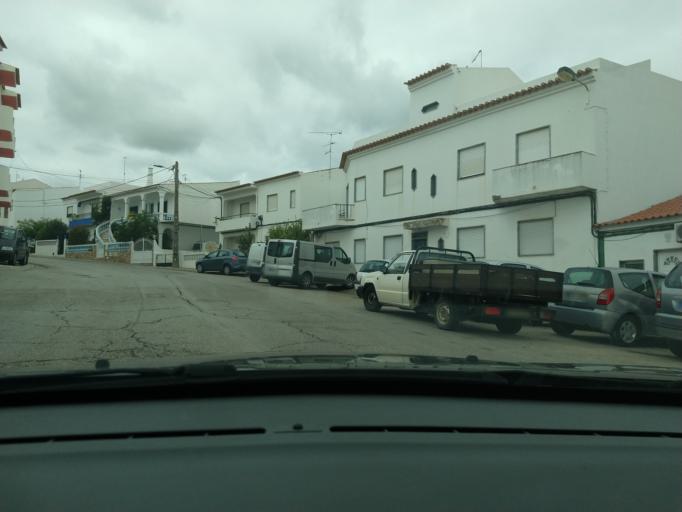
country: PT
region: Faro
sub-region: Lagoa
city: Lagoa
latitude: 37.1363
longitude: -8.4501
